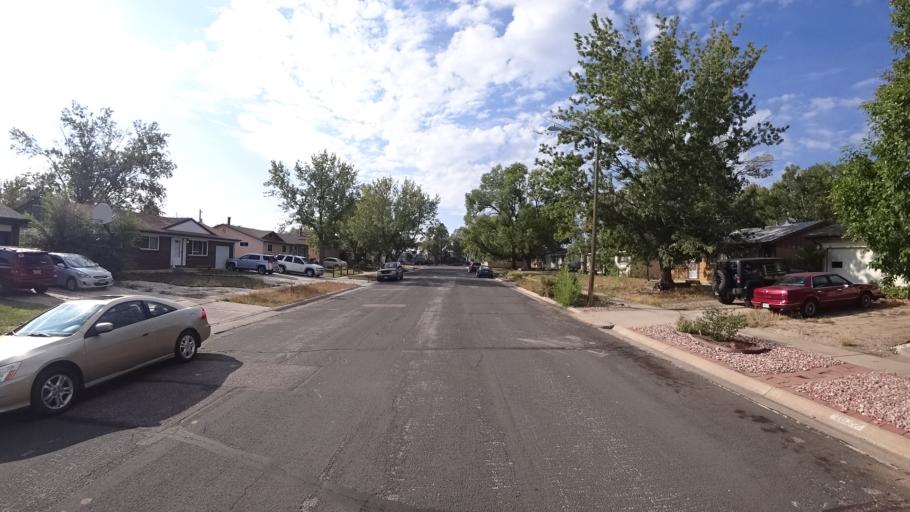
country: US
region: Colorado
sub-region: El Paso County
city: Cimarron Hills
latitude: 38.8561
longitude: -104.7591
